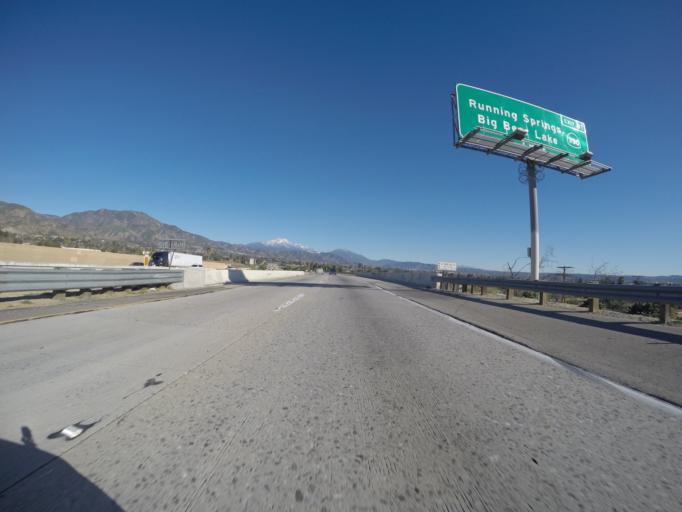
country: US
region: California
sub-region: San Bernardino County
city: Highland
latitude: 34.1323
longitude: -117.2274
